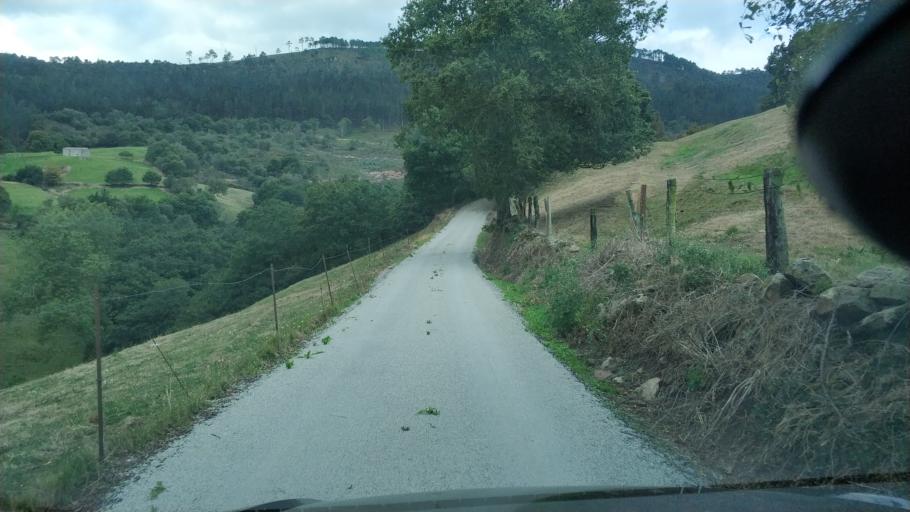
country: ES
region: Cantabria
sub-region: Provincia de Cantabria
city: Santa Maria de Cayon
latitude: 43.2888
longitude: -3.8555
